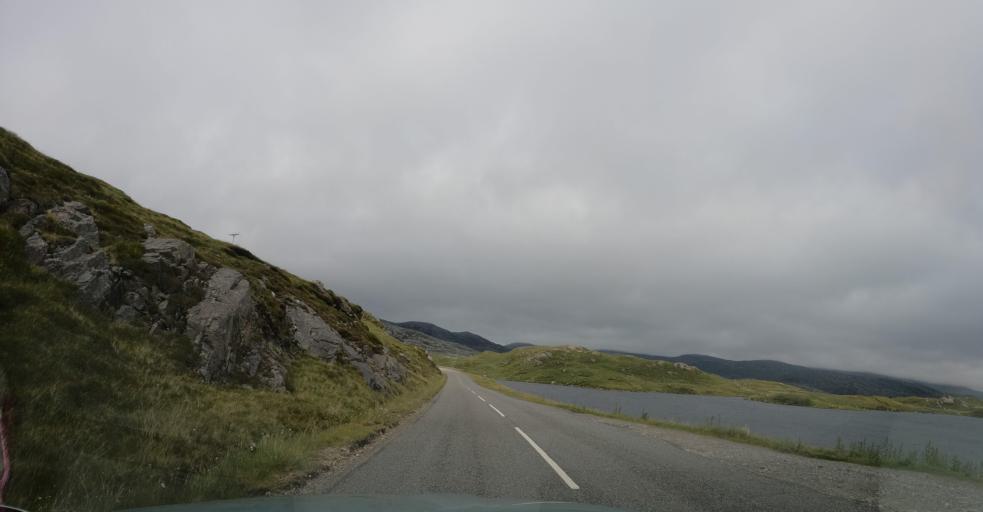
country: GB
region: Scotland
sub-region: Eilean Siar
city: Harris
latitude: 57.8893
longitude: -6.8031
